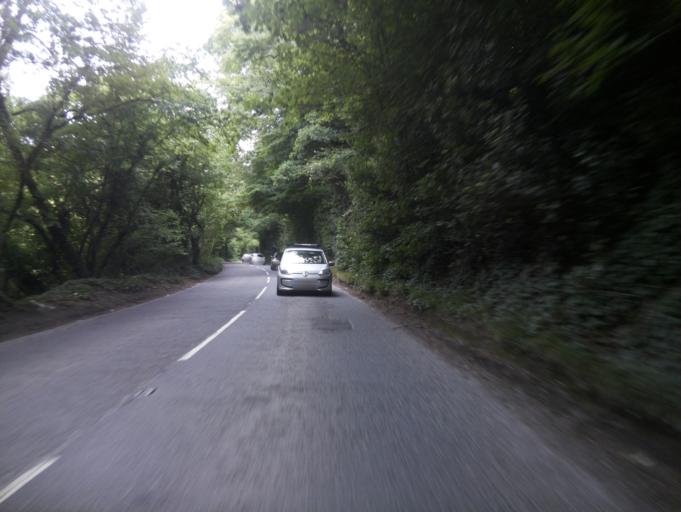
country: GB
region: England
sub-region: Somerset
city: Cheddar
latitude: 51.2929
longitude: -2.7892
